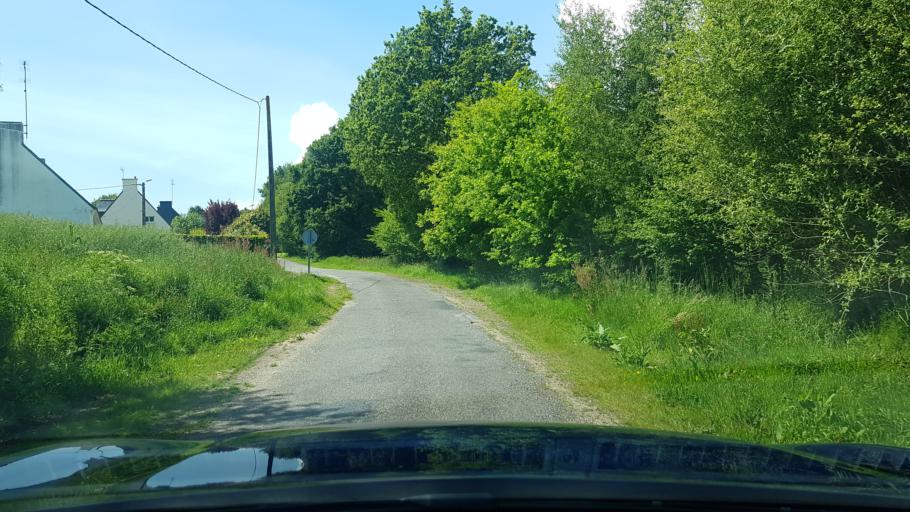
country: FR
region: Brittany
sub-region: Departement du Morbihan
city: Gestel
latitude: 47.8019
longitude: -3.4882
